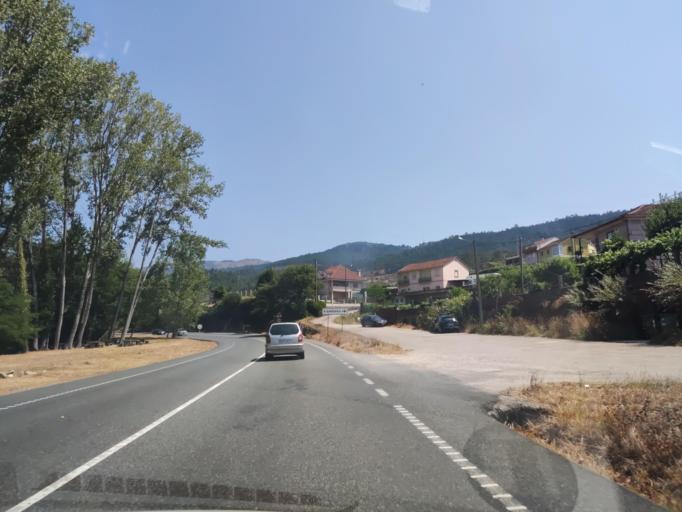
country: ES
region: Galicia
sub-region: Provincia de Pontevedra
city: Porrino
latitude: 42.1938
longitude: -8.6064
